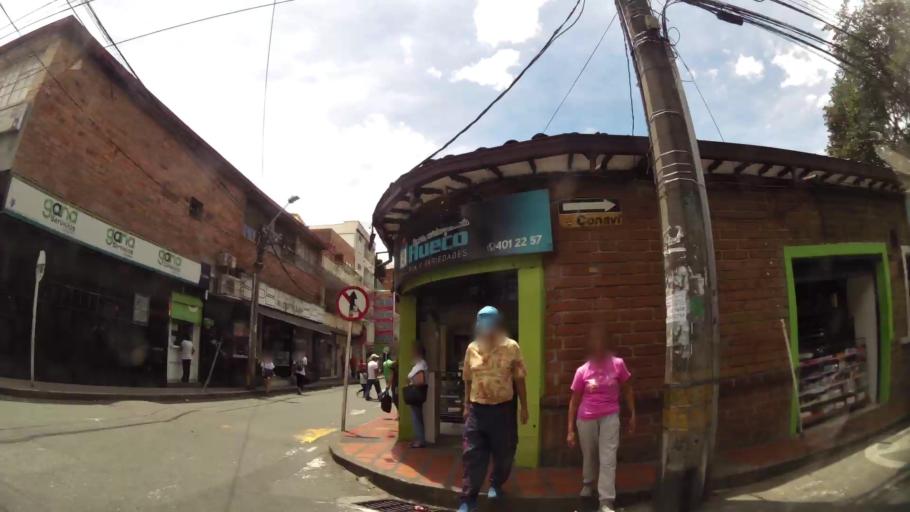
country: CO
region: Antioquia
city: Municipio de Copacabana
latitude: 6.3462
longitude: -75.5088
